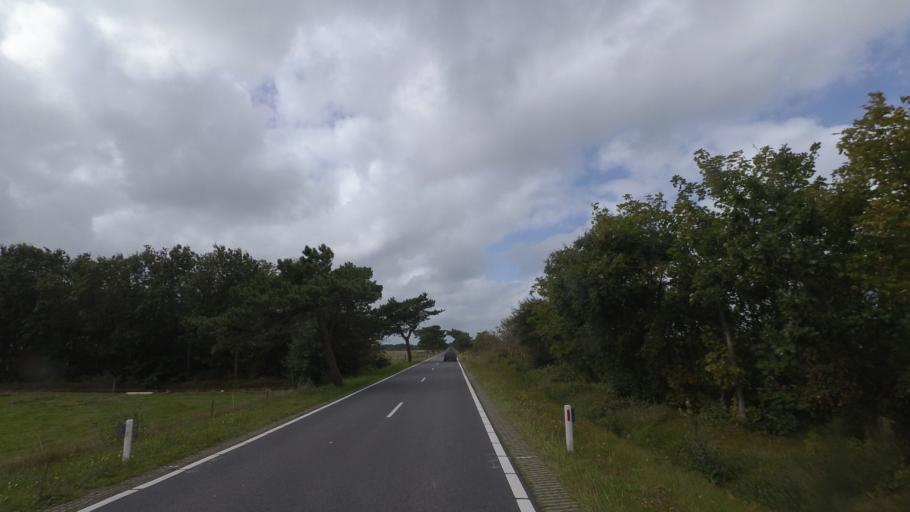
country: NL
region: Friesland
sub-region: Gemeente Ameland
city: Hollum
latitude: 53.4455
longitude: 5.6543
